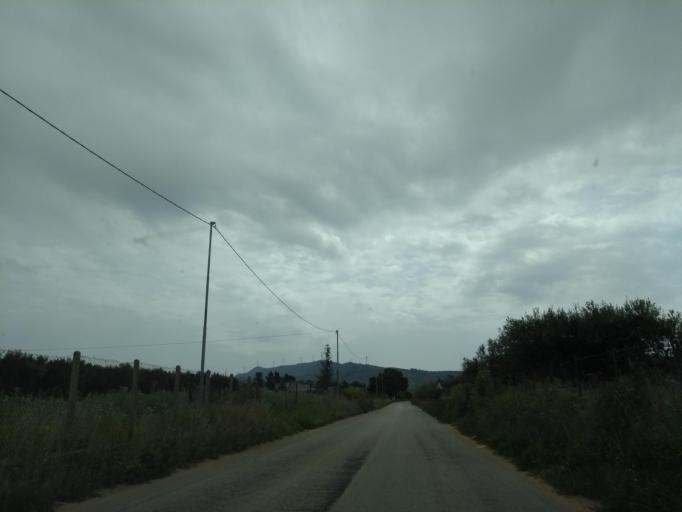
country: IT
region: Sicily
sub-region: Palermo
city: Partinico
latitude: 37.9979
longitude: 13.0651
